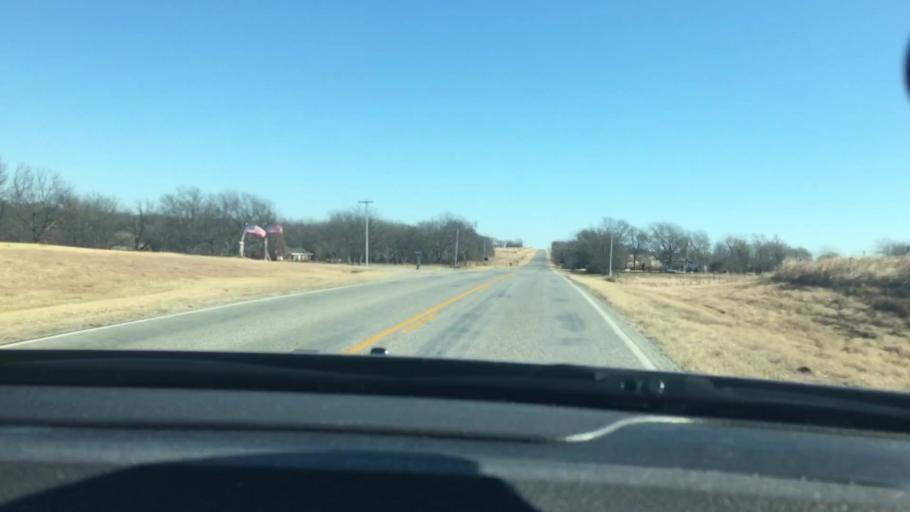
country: US
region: Oklahoma
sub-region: Garvin County
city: Wynnewood
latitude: 34.6514
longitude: -97.1054
